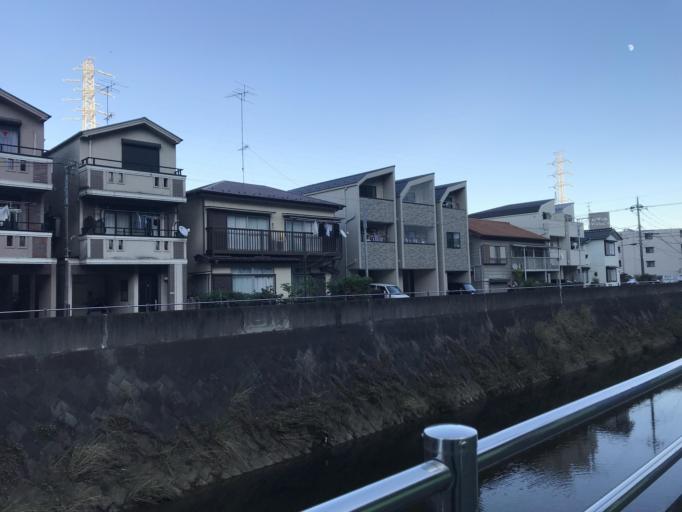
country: JP
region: Kanagawa
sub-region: Kawasaki-shi
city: Kawasaki
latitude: 35.5662
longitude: 139.6368
